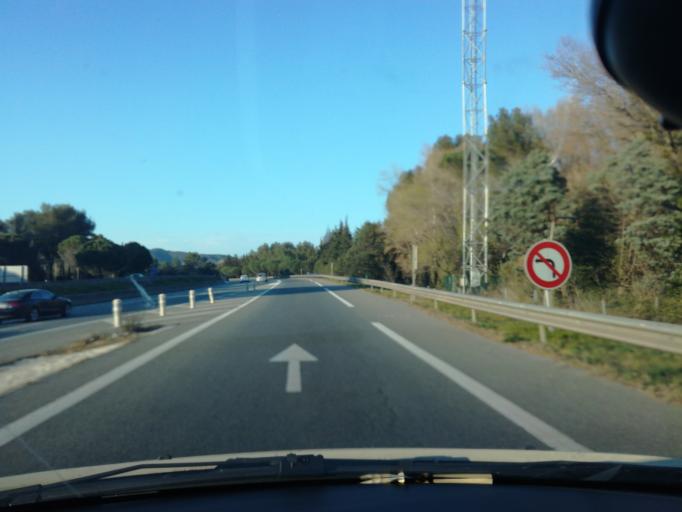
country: FR
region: Provence-Alpes-Cote d'Azur
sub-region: Departement du Var
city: Frejus
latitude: 43.4745
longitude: 6.7418
